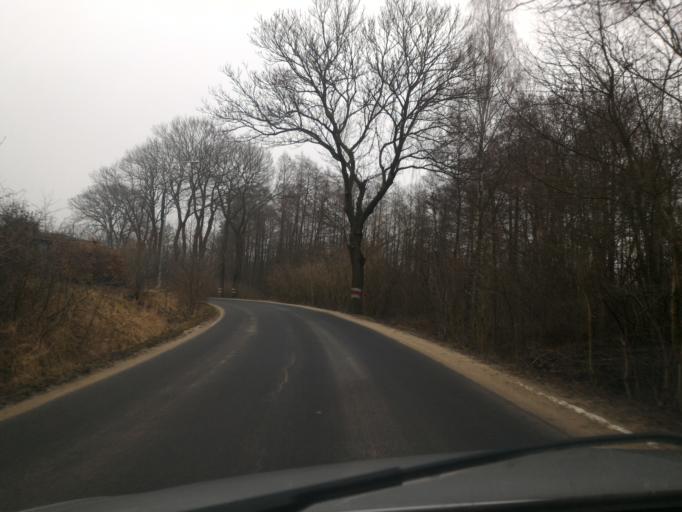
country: PL
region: Lower Silesian Voivodeship
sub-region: Powiat zgorzelecki
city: Bogatynia
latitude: 50.9083
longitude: 14.9903
